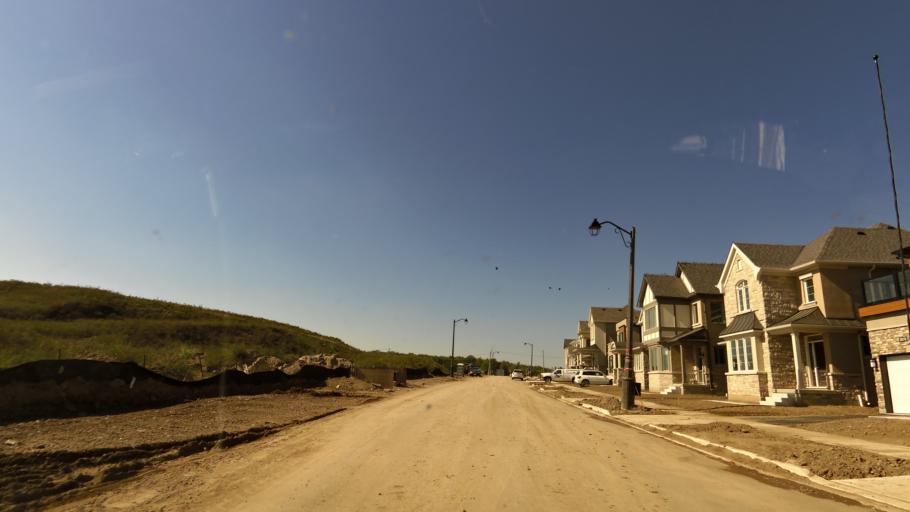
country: CA
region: Ontario
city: Oakville
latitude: 43.4732
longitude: -79.7452
